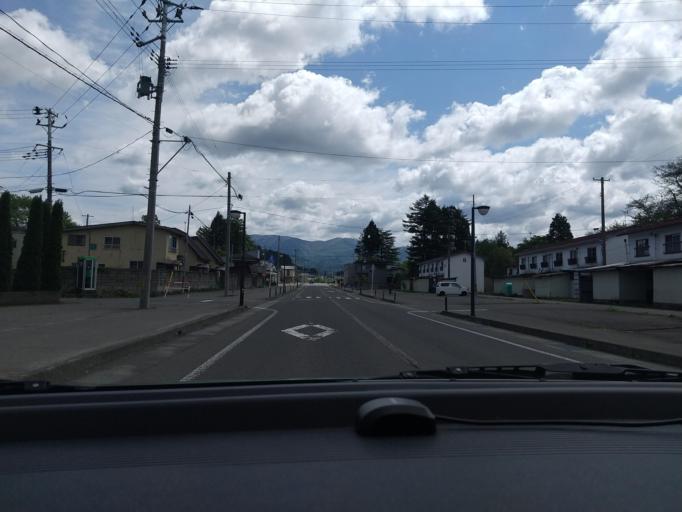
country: JP
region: Akita
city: Kakunodatemachi
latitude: 39.5846
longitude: 140.5616
